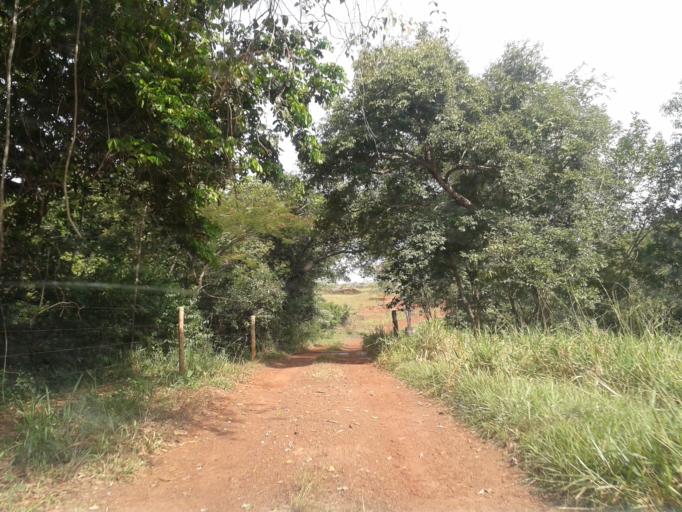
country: BR
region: Minas Gerais
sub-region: Campina Verde
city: Campina Verde
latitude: -19.4288
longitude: -49.7107
